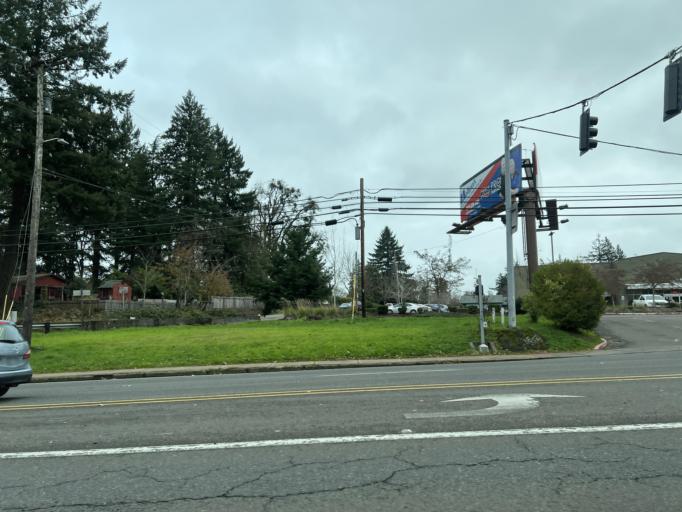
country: US
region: Oregon
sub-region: Marion County
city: Salem
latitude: 44.8932
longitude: -123.0360
